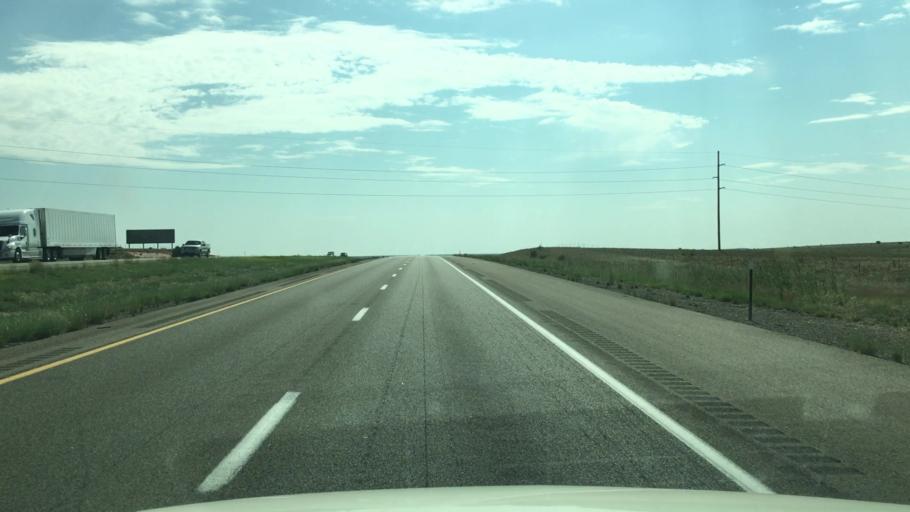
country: US
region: New Mexico
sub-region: Guadalupe County
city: Santa Rosa
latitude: 34.9781
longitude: -105.0269
